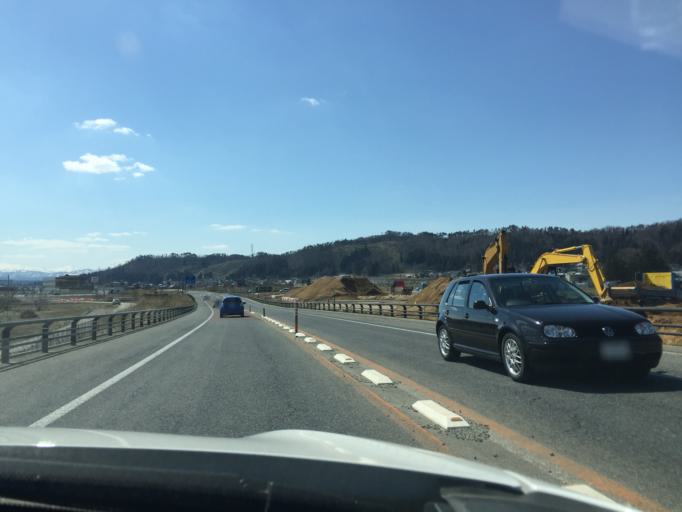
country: JP
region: Yamagata
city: Nagai
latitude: 38.0584
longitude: 140.1120
